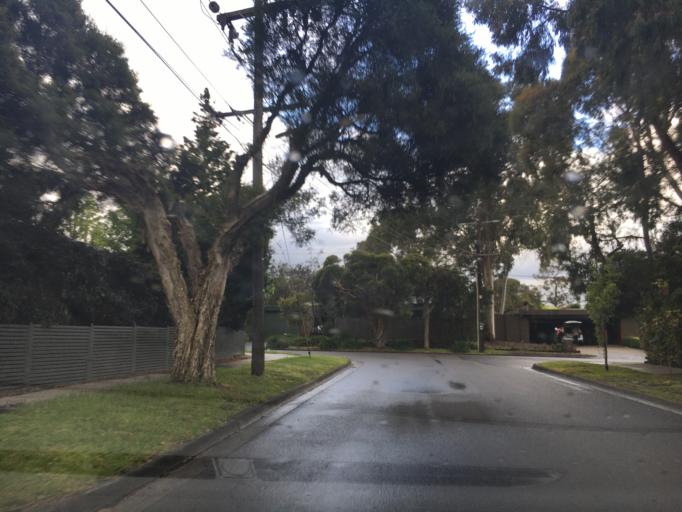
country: AU
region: Victoria
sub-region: Whitehorse
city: Vermont South
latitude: -37.8816
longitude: 145.1861
